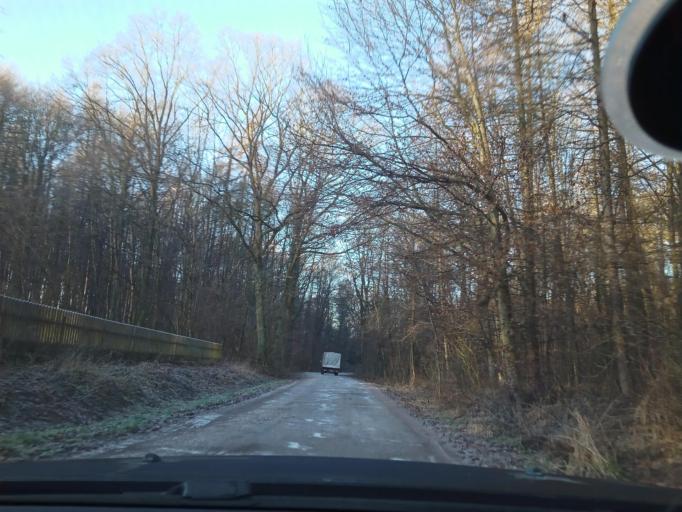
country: PL
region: Lesser Poland Voivodeship
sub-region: Powiat krakowski
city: Michalowice
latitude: 50.1895
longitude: 20.0375
